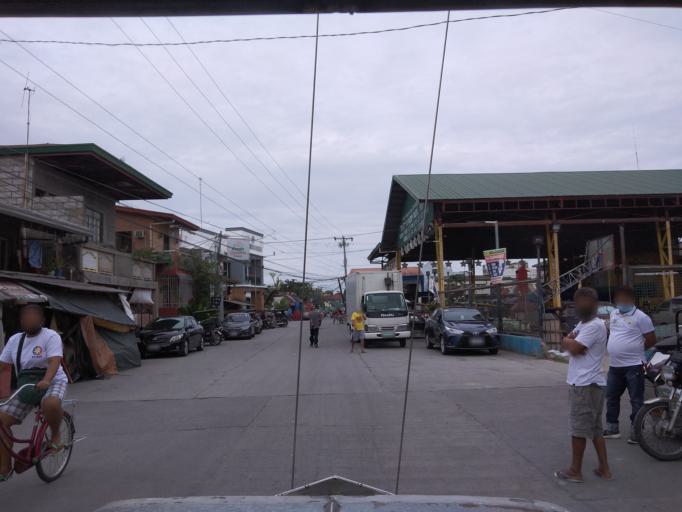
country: PH
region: Central Luzon
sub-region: Province of Pampanga
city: Sexmoan
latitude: 14.9360
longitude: 120.6227
